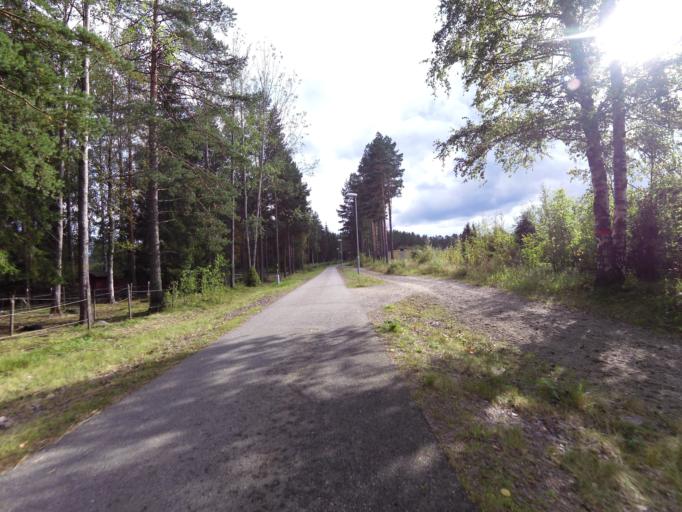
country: SE
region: Gaevleborg
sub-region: Sandvikens Kommun
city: Sandviken
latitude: 60.6808
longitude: 16.8167
